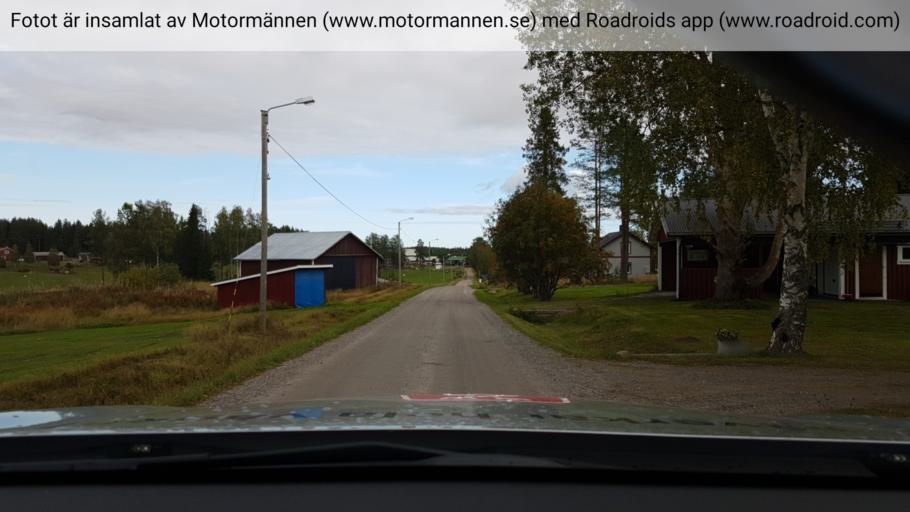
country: SE
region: Vaesterbotten
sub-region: Skelleftea Kommun
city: Byske
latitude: 65.1189
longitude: 21.2102
